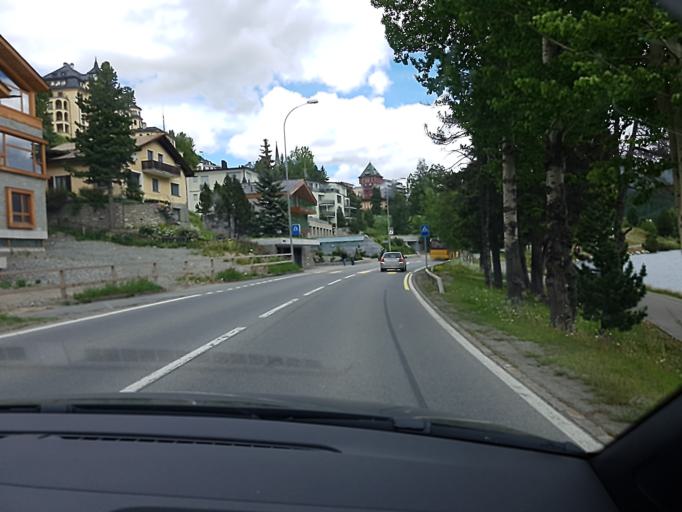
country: CH
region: Grisons
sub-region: Maloja District
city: Saint Moritz
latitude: 46.4932
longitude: 9.8362
